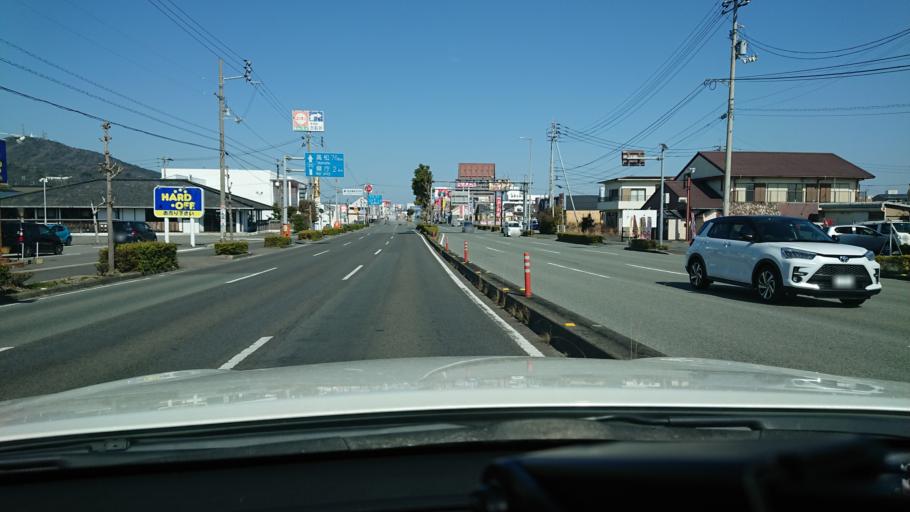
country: JP
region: Tokushima
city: Tokushima-shi
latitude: 34.0457
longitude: 134.5520
